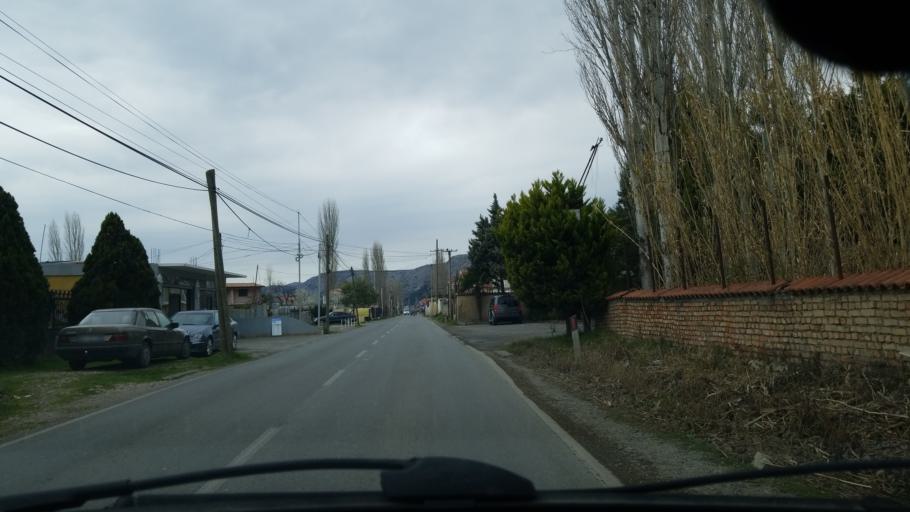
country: AL
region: Lezhe
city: Lezhe
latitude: 41.7824
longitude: 19.6304
